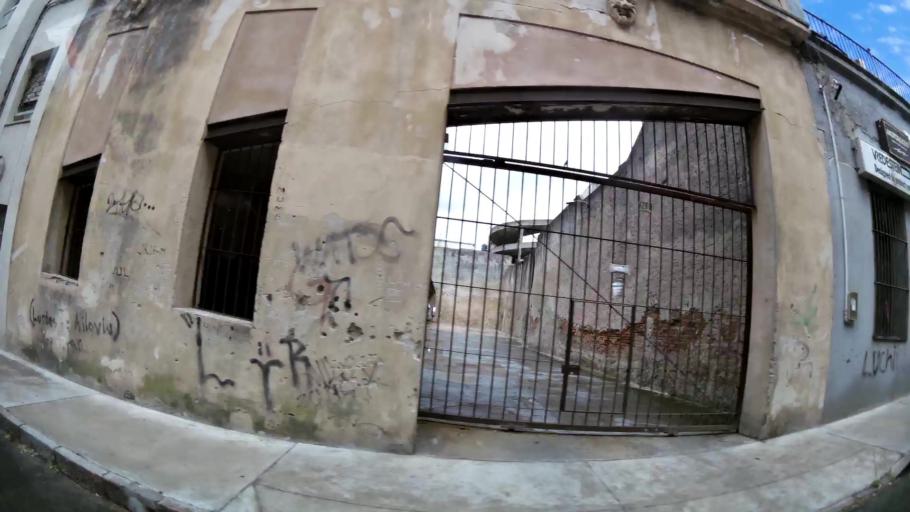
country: UY
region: Montevideo
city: Montevideo
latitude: -34.9095
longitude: -56.2062
